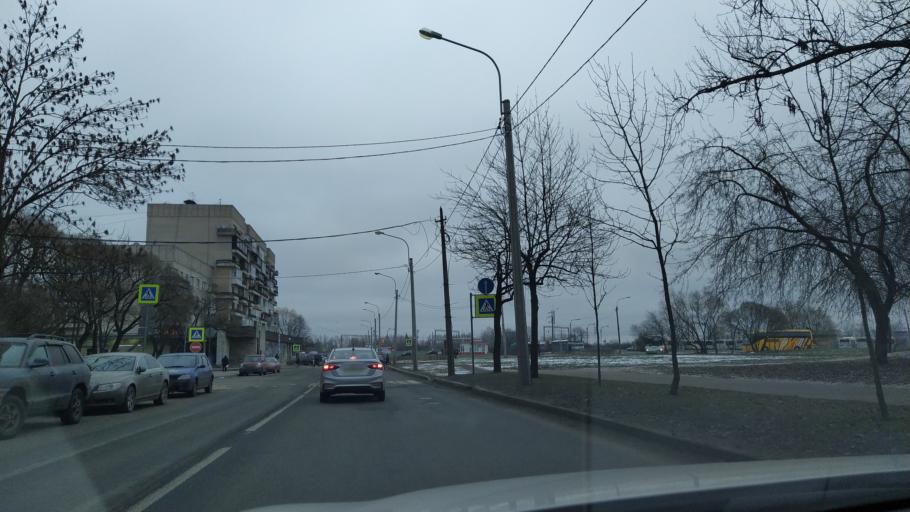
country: RU
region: St.-Petersburg
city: Pushkin
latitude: 59.7295
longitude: 30.4212
